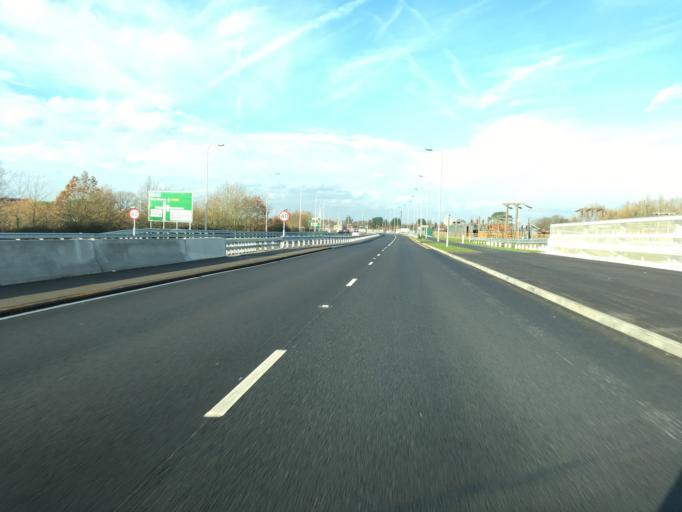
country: GB
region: England
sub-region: Cheshire East
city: Wilmslow
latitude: 53.3604
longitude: -2.2404
